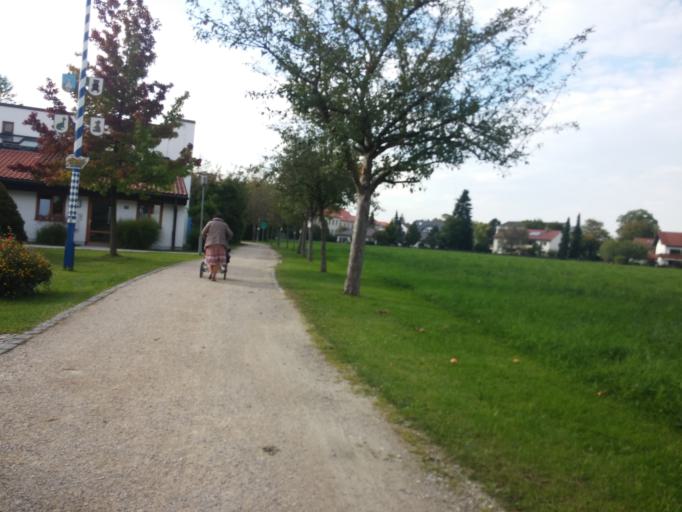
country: DE
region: Bavaria
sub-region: Upper Bavaria
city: Feldkirchen
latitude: 48.1454
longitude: 11.7344
